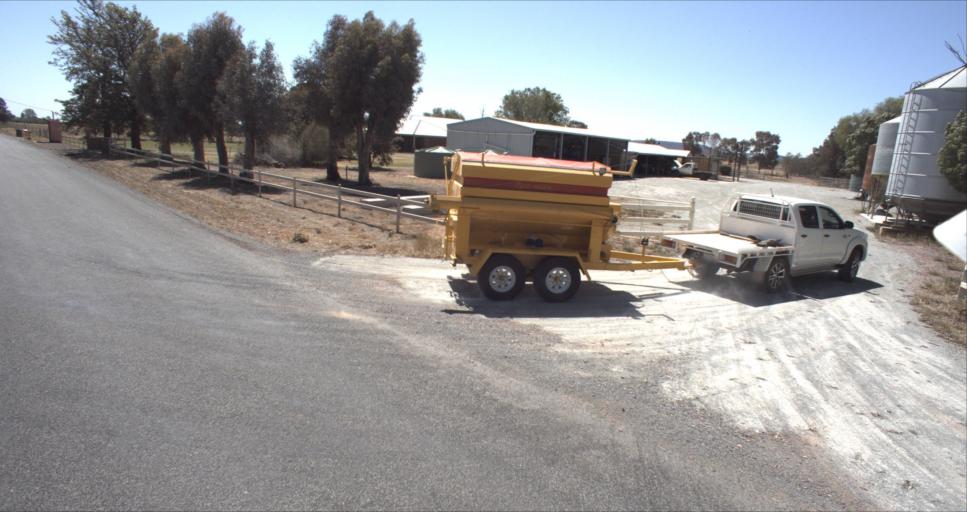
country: AU
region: New South Wales
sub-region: Leeton
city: Leeton
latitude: -34.5230
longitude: 146.4414
